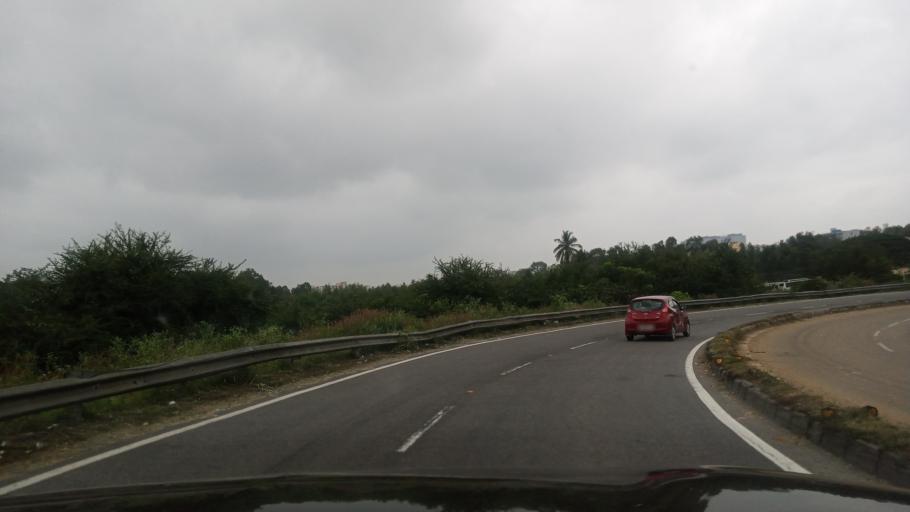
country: IN
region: Karnataka
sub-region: Bangalore Urban
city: Bangalore
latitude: 12.8585
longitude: 77.6642
